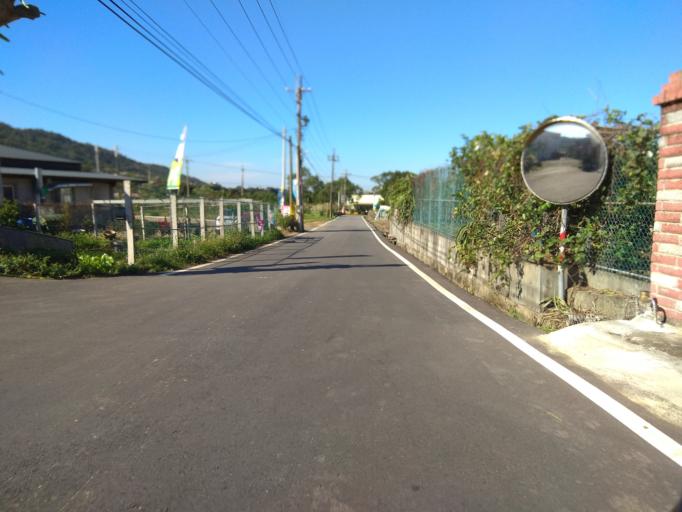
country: TW
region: Taiwan
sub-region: Hsinchu
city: Zhubei
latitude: 24.8443
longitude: 121.1254
